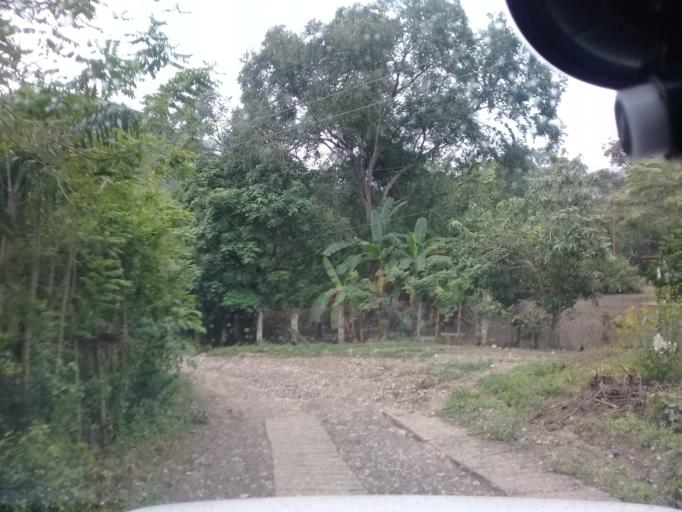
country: MX
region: Veracruz
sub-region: Chalma
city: San Pedro Coyutla
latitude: 21.2429
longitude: -98.4202
